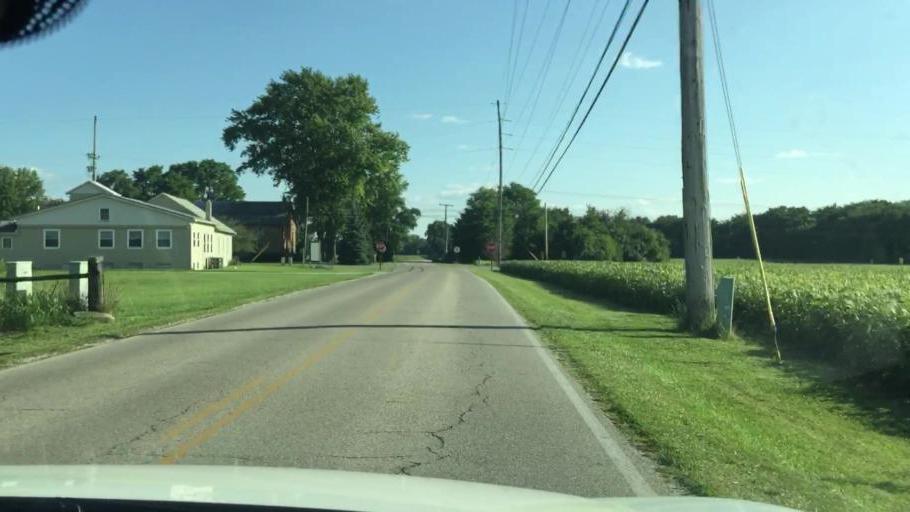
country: US
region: Ohio
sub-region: Clark County
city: Northridge
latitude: 39.9400
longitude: -83.7105
